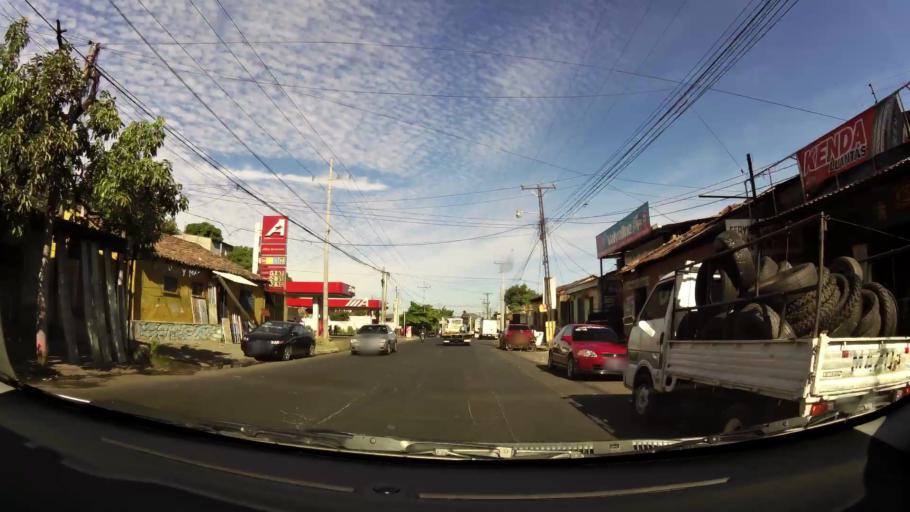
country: SV
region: Santa Ana
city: Santa Ana
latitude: 13.9831
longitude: -89.5734
